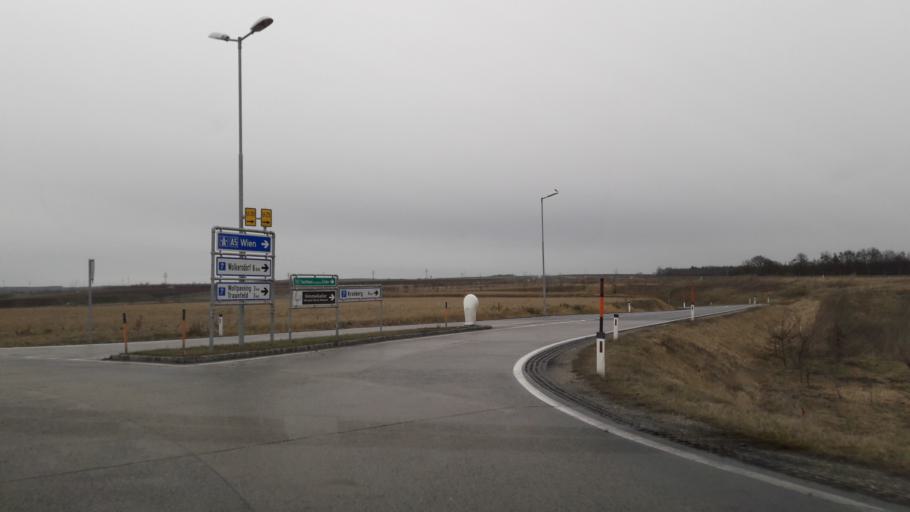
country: AT
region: Lower Austria
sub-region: Politischer Bezirk Mistelbach
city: Hochleithen
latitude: 48.4273
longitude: 16.5510
